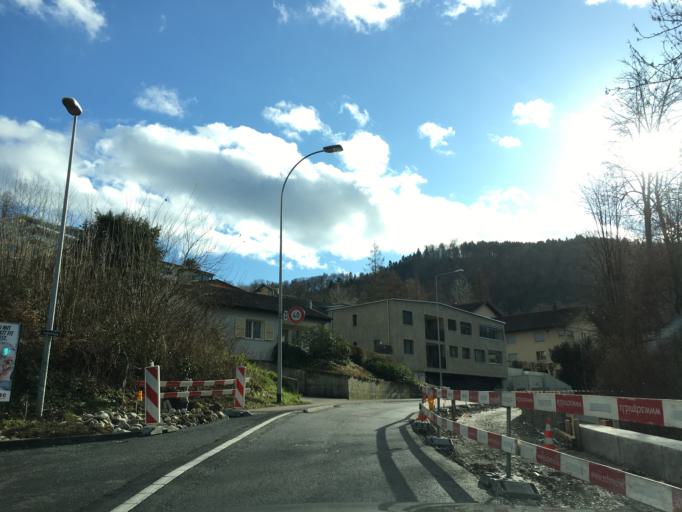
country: CH
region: Lucerne
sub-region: Lucerne-Land District
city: Ebikon
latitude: 47.0753
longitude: 8.3380
